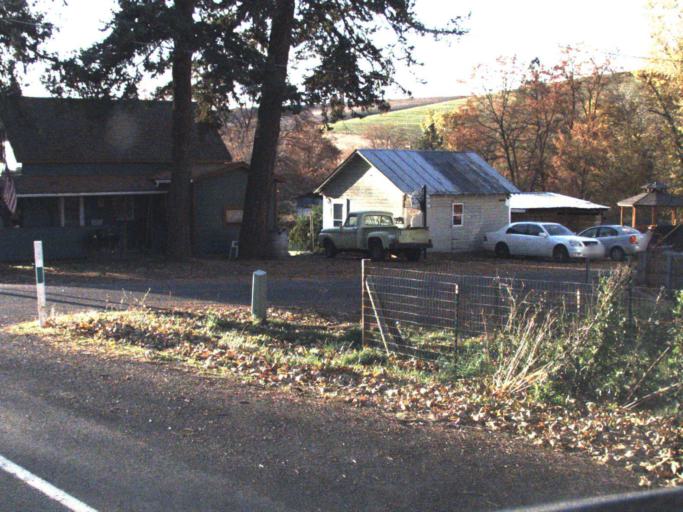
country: US
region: Washington
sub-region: Walla Walla County
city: Waitsburg
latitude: 46.1402
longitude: -118.1552
